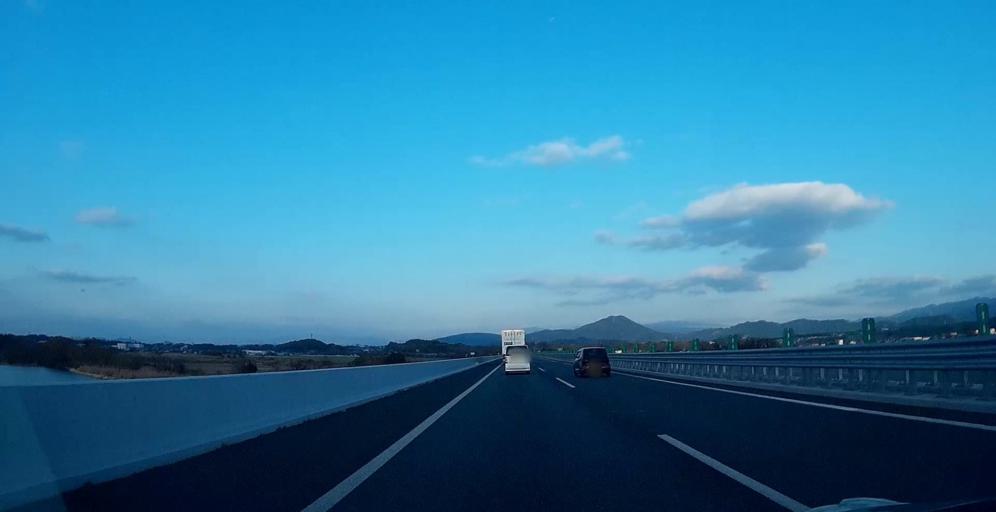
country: JP
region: Kumamoto
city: Uto
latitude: 32.7120
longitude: 130.7616
